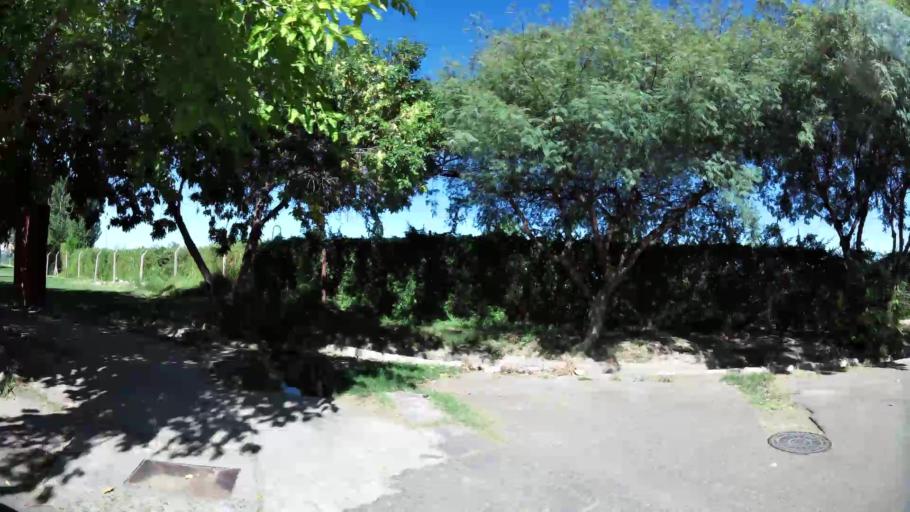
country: AR
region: Mendoza
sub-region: Departamento de Godoy Cruz
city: Godoy Cruz
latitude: -32.9487
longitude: -68.8127
